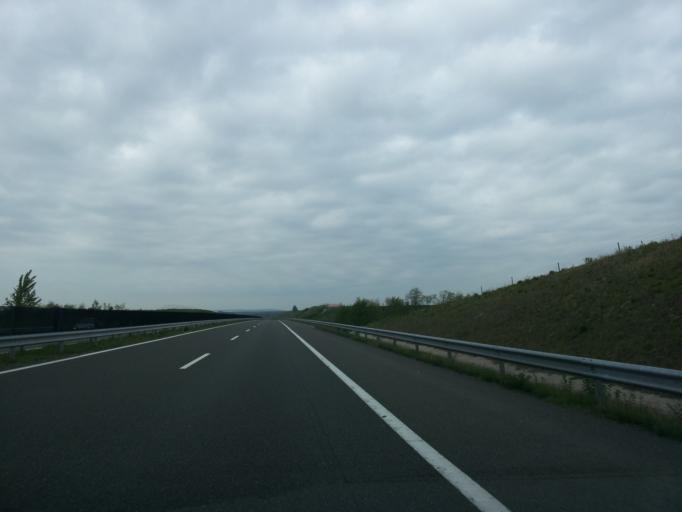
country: HU
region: Tolna
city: Paks
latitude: 46.6893
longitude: 18.8397
